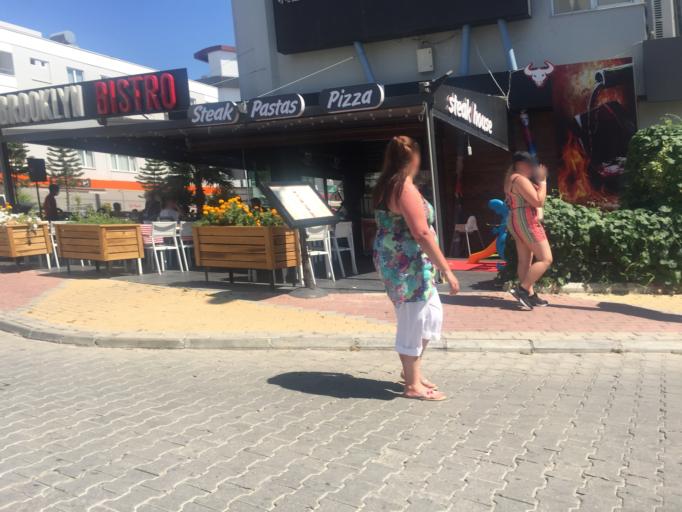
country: TR
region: Antalya
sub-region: Alanya
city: Alanya
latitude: 36.5370
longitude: 32.0362
